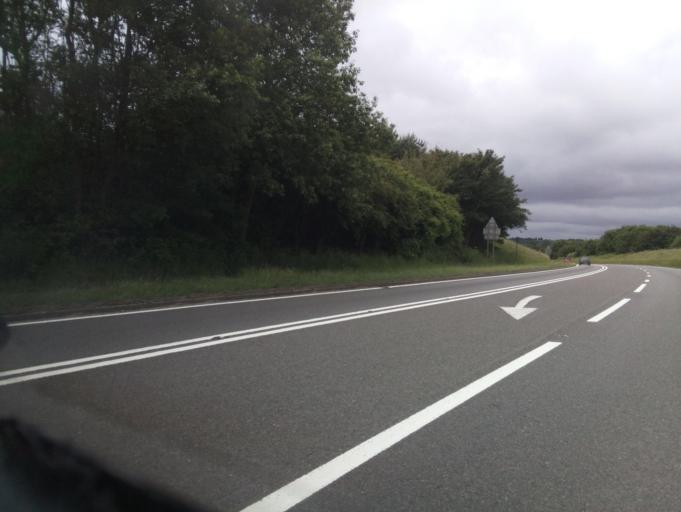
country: GB
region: England
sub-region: Leicestershire
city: Ashby de la Zouch
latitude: 52.7641
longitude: -1.4673
